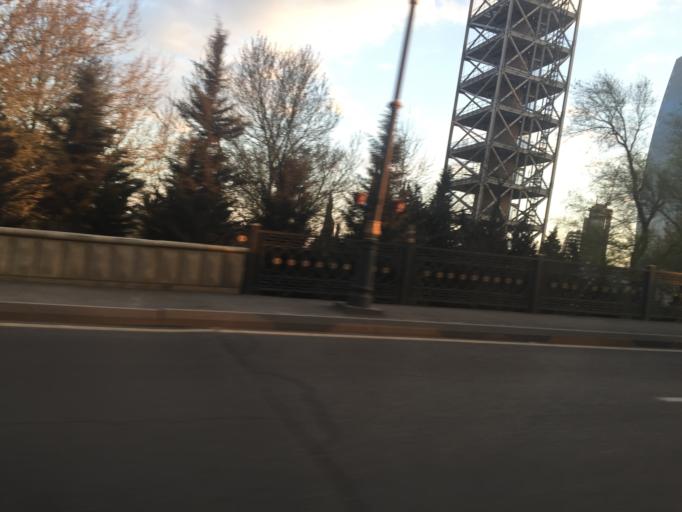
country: AZ
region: Baki
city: Baku
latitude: 40.3775
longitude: 49.8644
